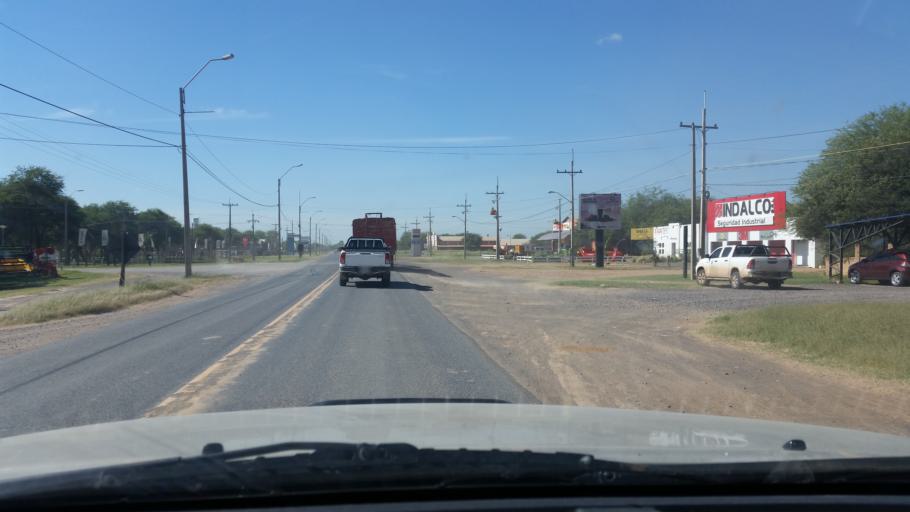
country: PY
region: Boqueron
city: Colonia Menno
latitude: -22.3895
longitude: -59.8365
